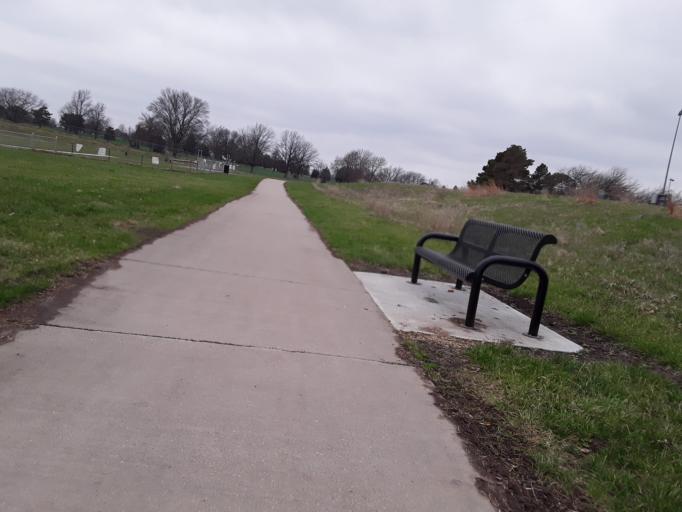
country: US
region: Nebraska
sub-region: Lancaster County
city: Lincoln
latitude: 40.8492
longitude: -96.6082
